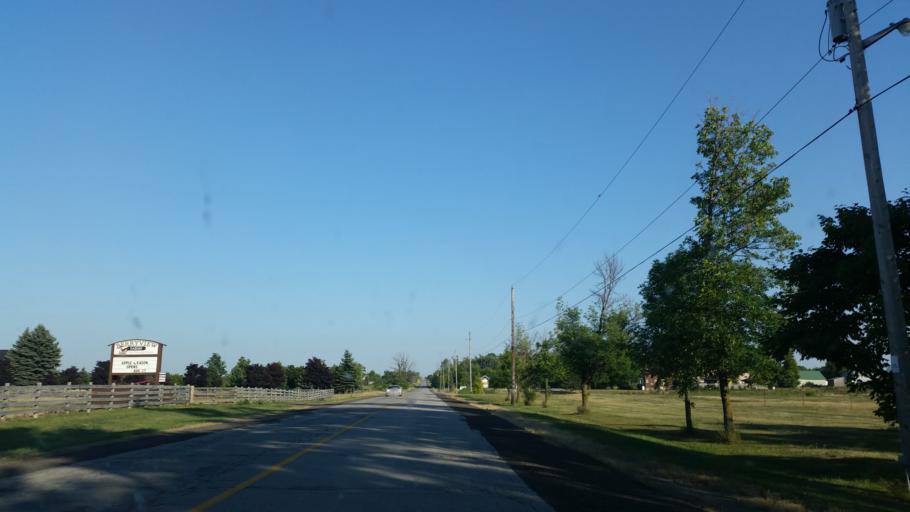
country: CA
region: Ontario
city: Brampton
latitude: 43.7877
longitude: -79.8505
